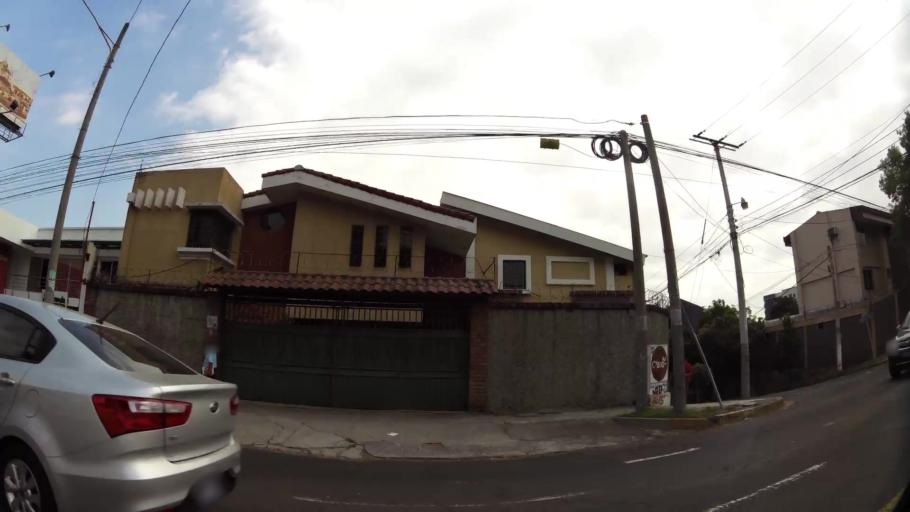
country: SV
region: La Libertad
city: Antiguo Cuscatlan
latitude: 13.7099
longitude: -89.2483
